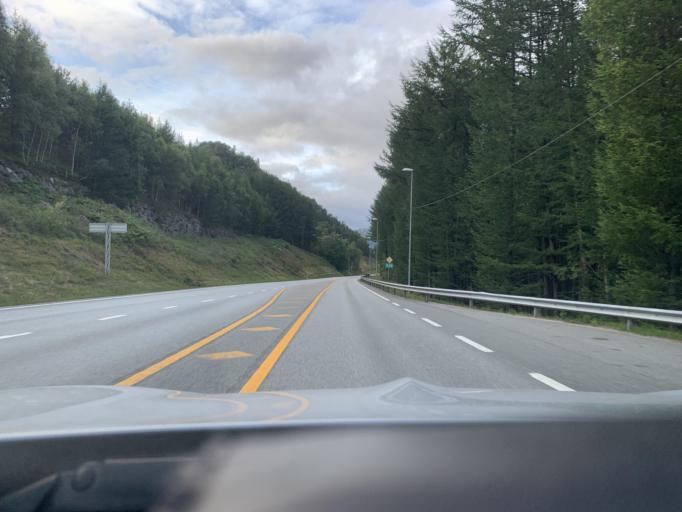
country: NO
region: Rogaland
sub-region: Bjerkreim
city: Vikesa
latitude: 58.5952
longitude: 6.0794
